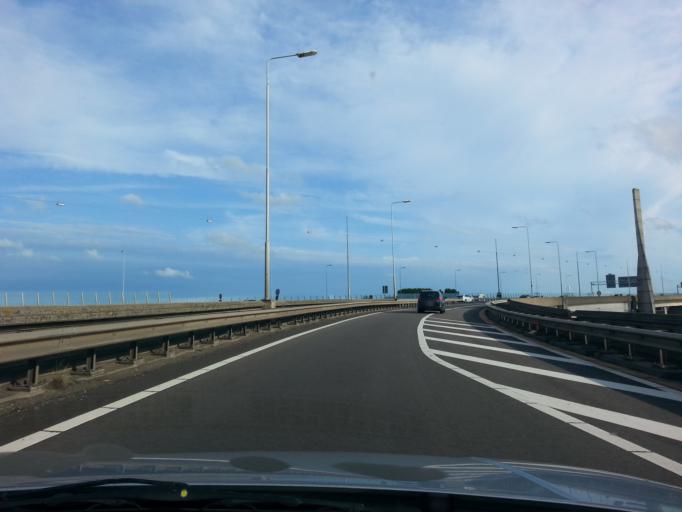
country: NL
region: North Holland
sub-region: Gemeente Diemen
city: Diemen
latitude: 52.3652
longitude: 4.9703
